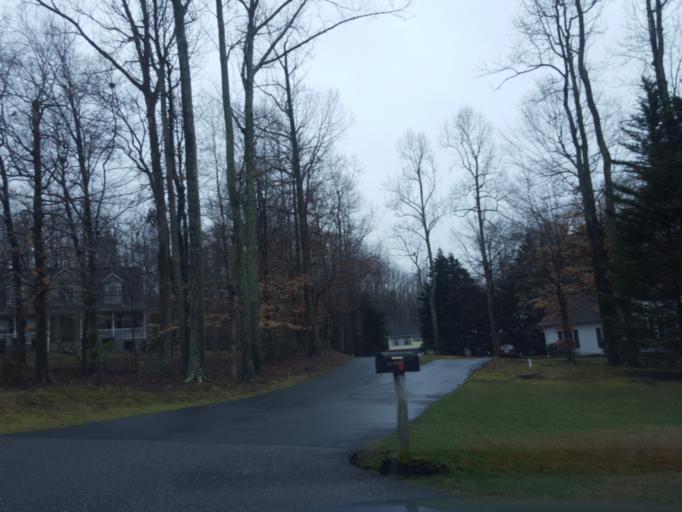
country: US
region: Maryland
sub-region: Calvert County
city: Huntingtown
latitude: 38.6037
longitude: -76.5400
